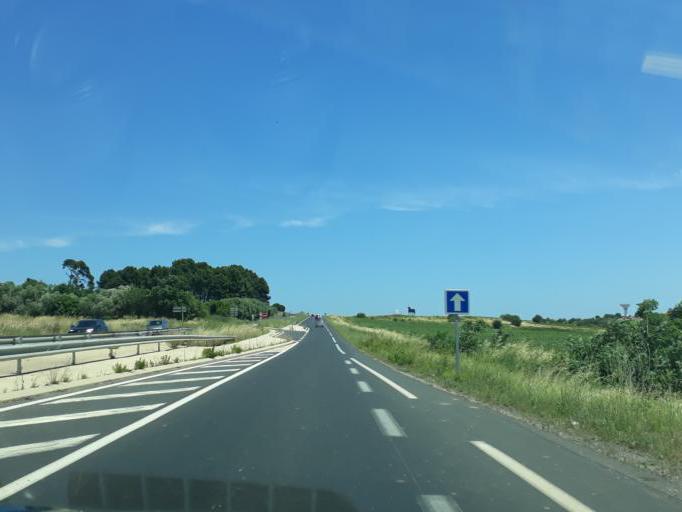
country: FR
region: Languedoc-Roussillon
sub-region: Departement de l'Herault
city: Cers
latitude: 43.3143
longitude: 3.3161
